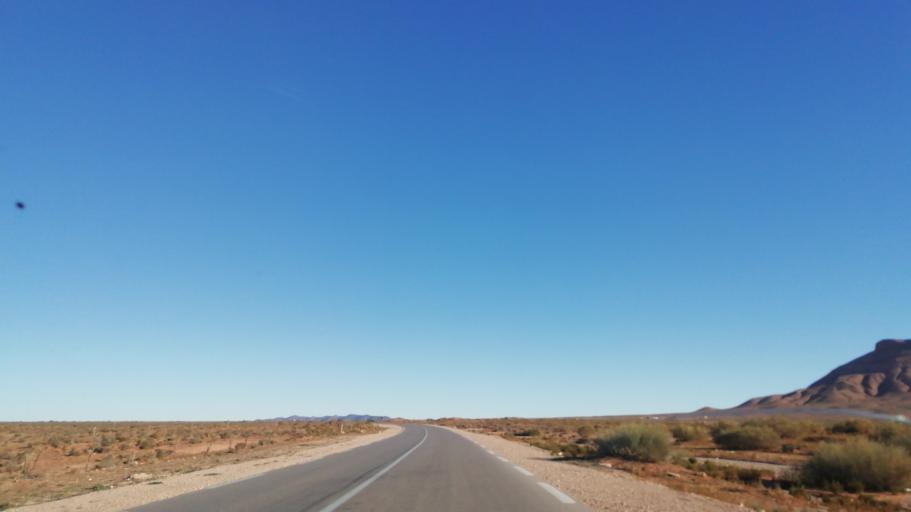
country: DZ
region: El Bayadh
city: El Abiodh Sidi Cheikh
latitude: 33.1126
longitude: 0.2514
